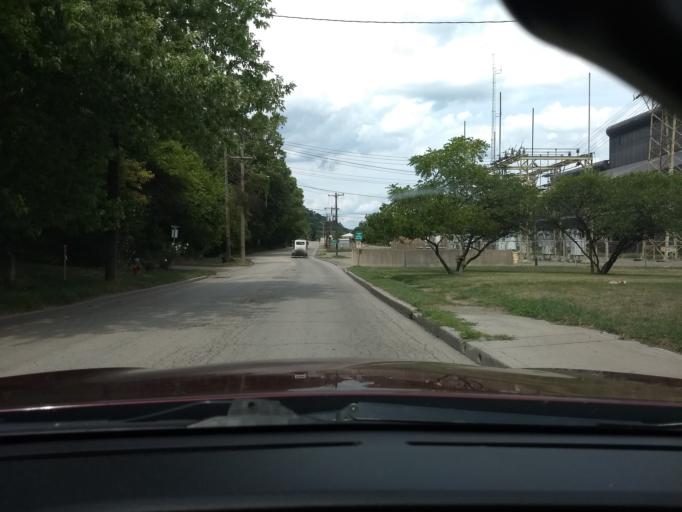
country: US
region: Pennsylvania
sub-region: Allegheny County
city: Brackenridge
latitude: 40.6191
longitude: -79.7195
